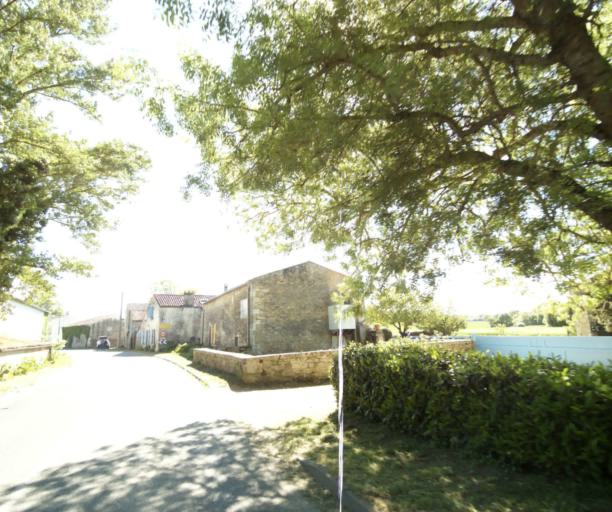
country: FR
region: Poitou-Charentes
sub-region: Departement de la Charente-Maritime
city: Bussac-sur-Charente
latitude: 45.8243
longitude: -0.6576
